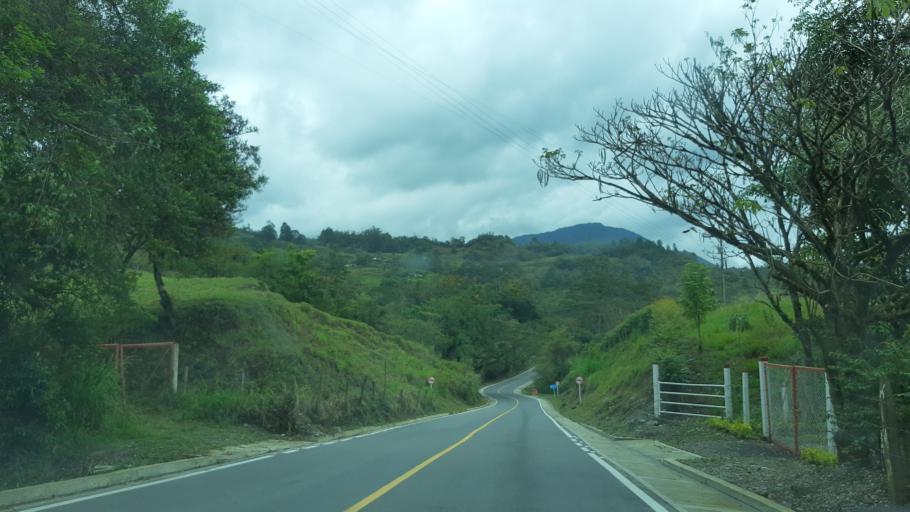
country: CO
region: Boyaca
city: Chivor
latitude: 4.9652
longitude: -73.3241
